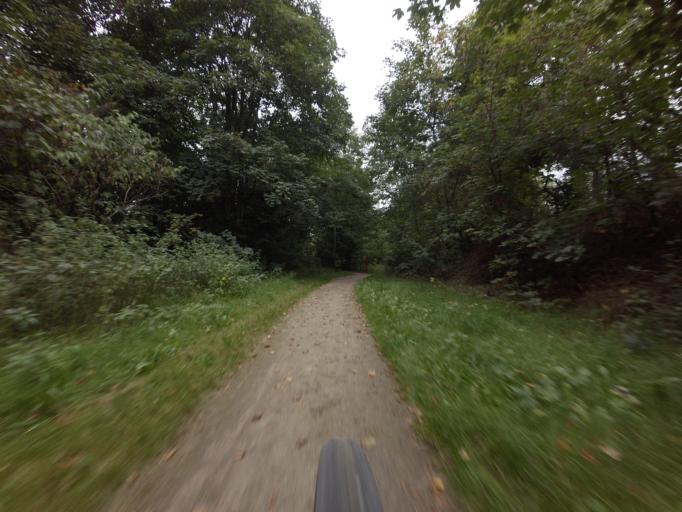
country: DK
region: South Denmark
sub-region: Billund Kommune
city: Billund
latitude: 55.8130
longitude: 9.0264
